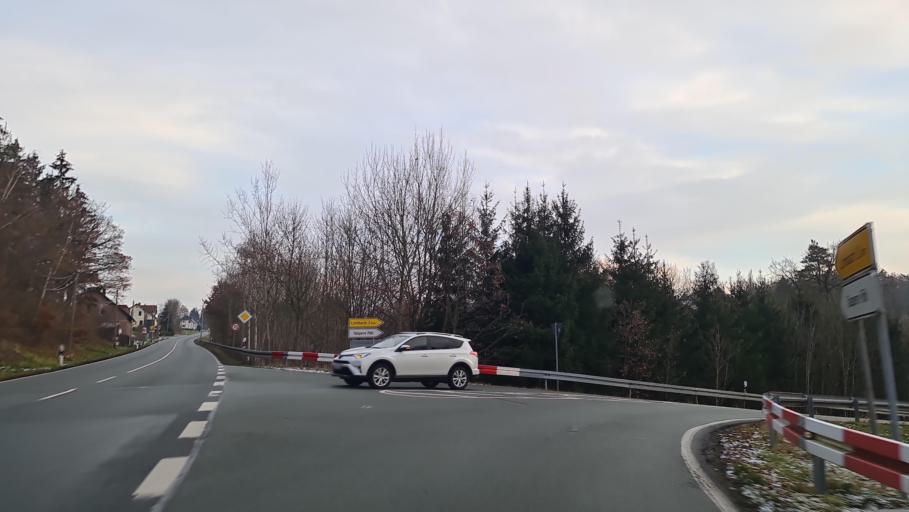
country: DE
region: Saxony
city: Limbach
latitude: 50.5988
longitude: 12.2586
